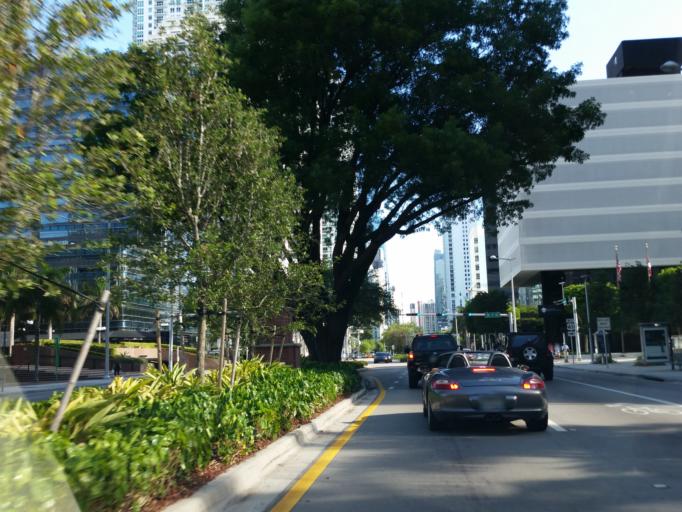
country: US
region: Florida
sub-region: Miami-Dade County
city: Miami
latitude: 25.7678
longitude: -80.1904
